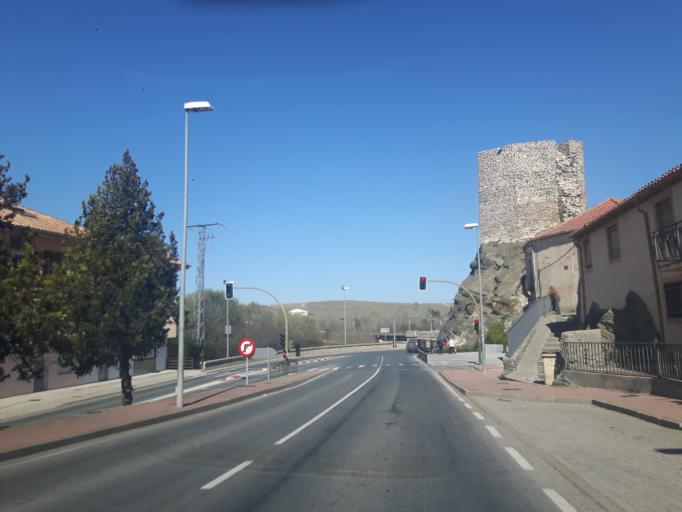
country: ES
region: Castille and Leon
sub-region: Provincia de Salamanca
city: Alba de Tormes
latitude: 40.8241
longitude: -5.5155
